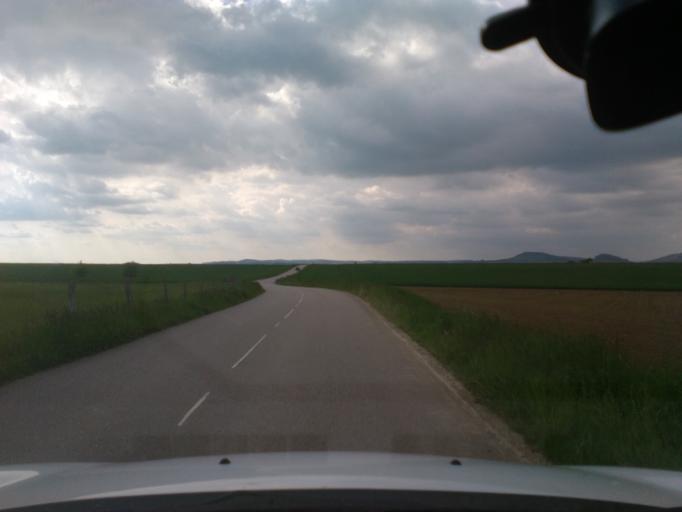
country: FR
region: Lorraine
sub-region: Departement des Vosges
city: Mirecourt
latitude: 48.3233
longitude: 6.1152
